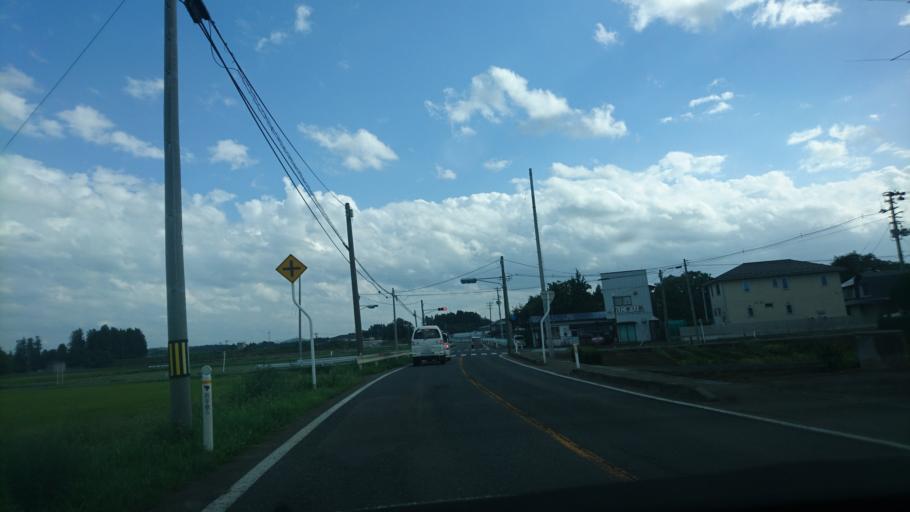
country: JP
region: Iwate
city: Hanamaki
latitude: 39.4694
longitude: 141.1668
